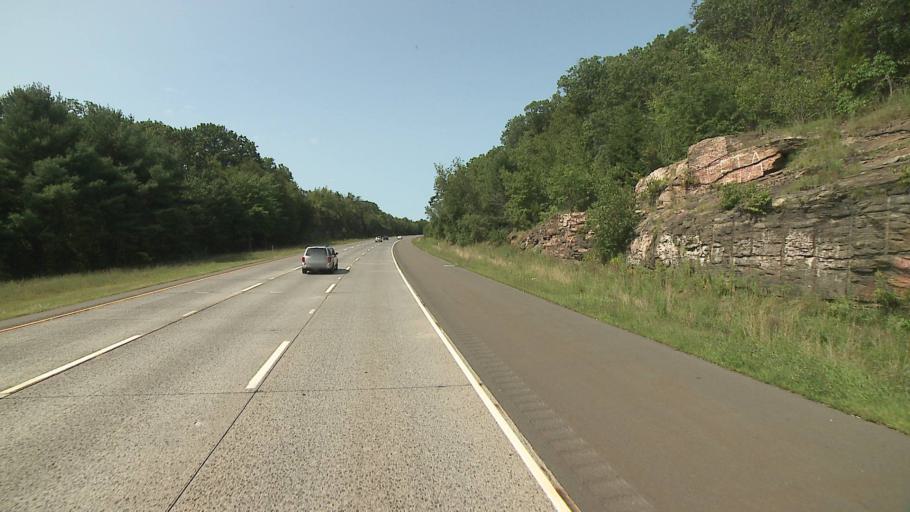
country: US
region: Connecticut
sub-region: Fairfield County
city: Trumbull
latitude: 41.2579
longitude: -73.2058
